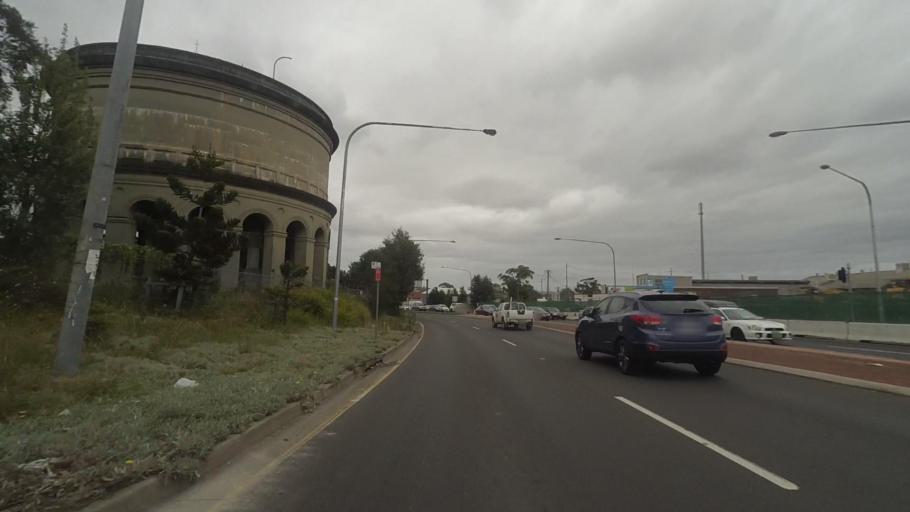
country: AU
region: New South Wales
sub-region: Bankstown
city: Bankstown
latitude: -33.9058
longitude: 151.0401
